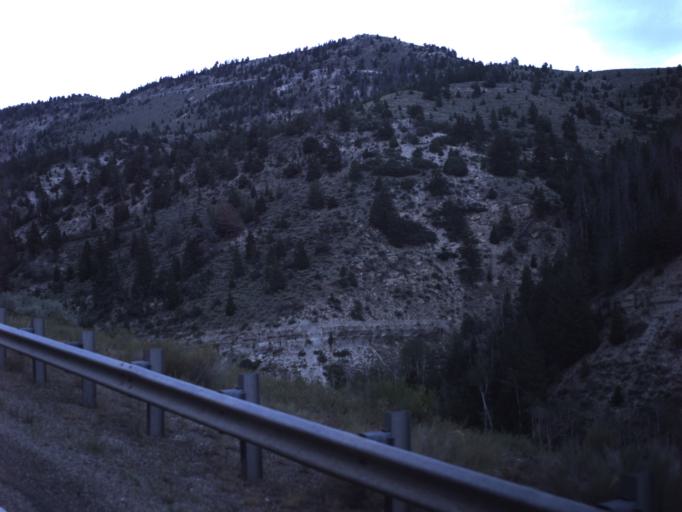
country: US
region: Utah
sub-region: Carbon County
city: Helper
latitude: 39.8501
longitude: -110.7660
